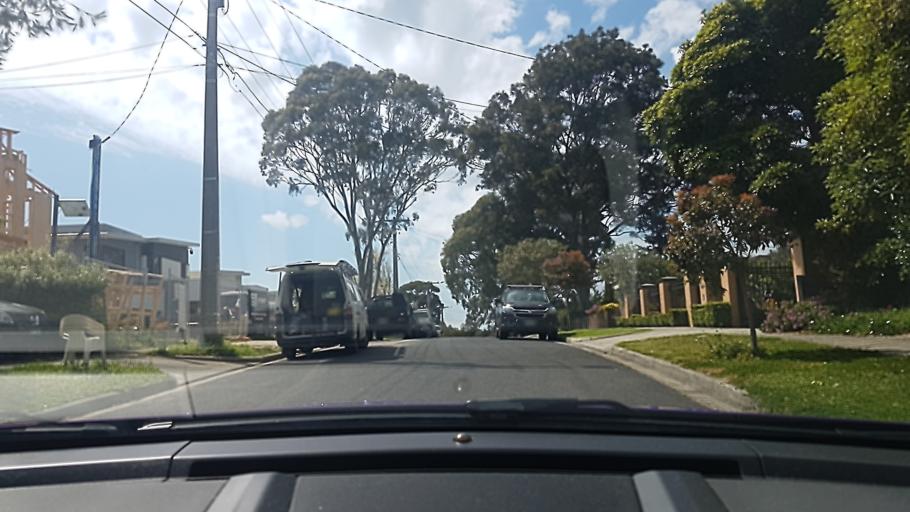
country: AU
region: Victoria
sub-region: Banyule
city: Darch
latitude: -37.7572
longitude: 145.1062
